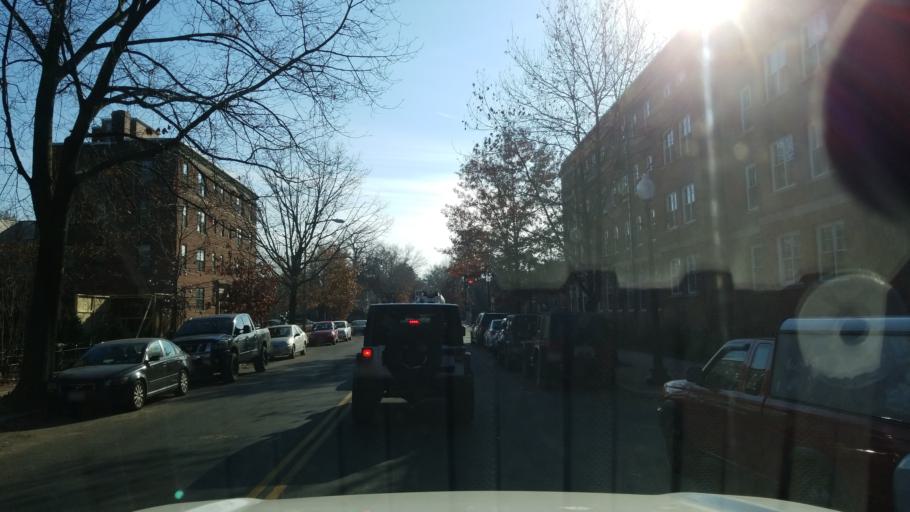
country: US
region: Washington, D.C.
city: Washington, D.C.
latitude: 38.8928
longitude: -76.9949
